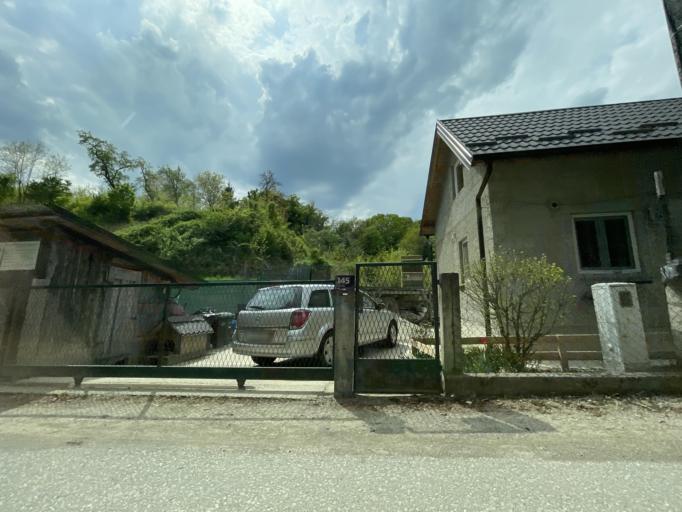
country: HR
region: Grad Zagreb
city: Zagreb
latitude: 45.8366
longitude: 15.9442
